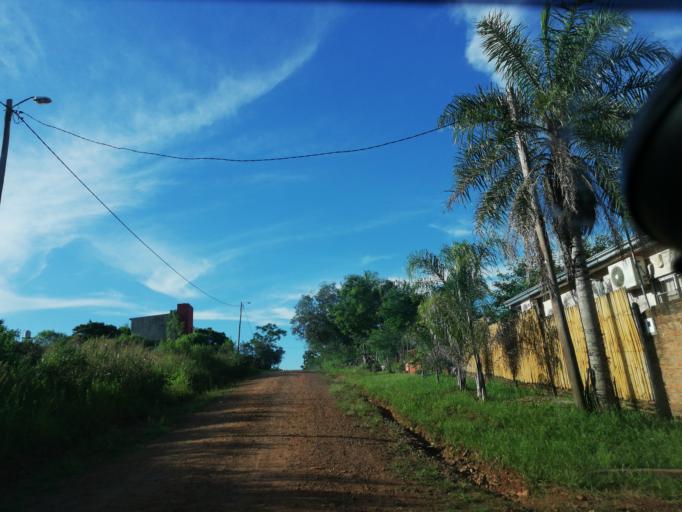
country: AR
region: Misiones
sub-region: Departamento de Capital
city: Posadas
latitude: -27.4012
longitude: -55.9598
